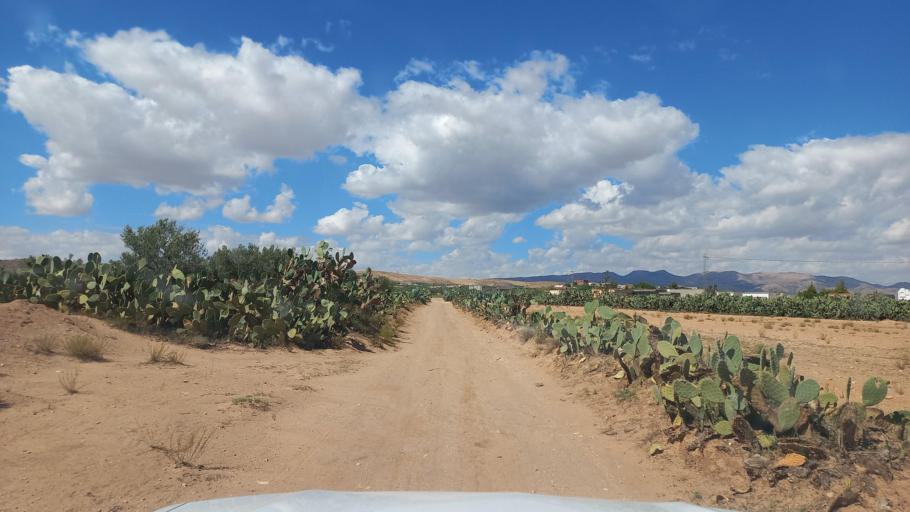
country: TN
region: Al Qasrayn
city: Sbiba
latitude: 35.3550
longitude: 9.0186
